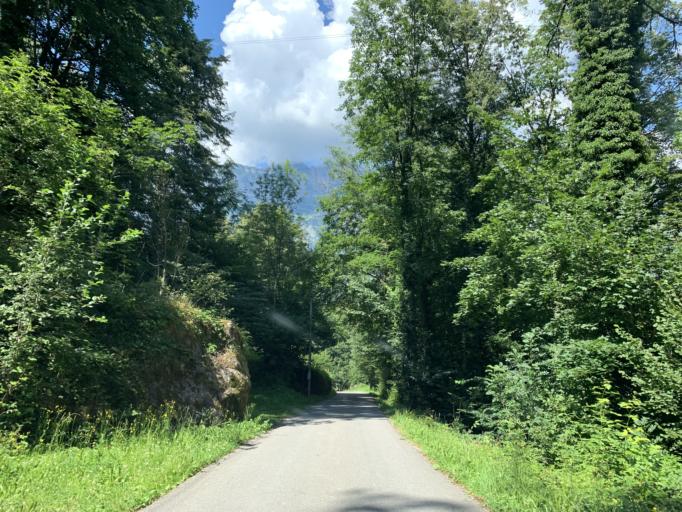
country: CH
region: Saint Gallen
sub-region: Wahlkreis Sarganserland
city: Quarten
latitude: 47.1064
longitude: 9.2129
